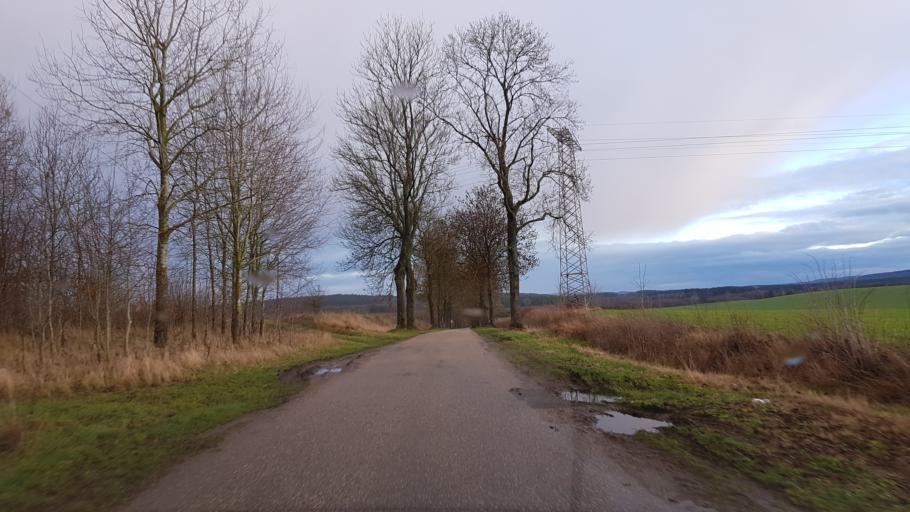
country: PL
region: West Pomeranian Voivodeship
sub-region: Powiat swidwinski
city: Rabino
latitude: 53.9436
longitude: 15.9280
